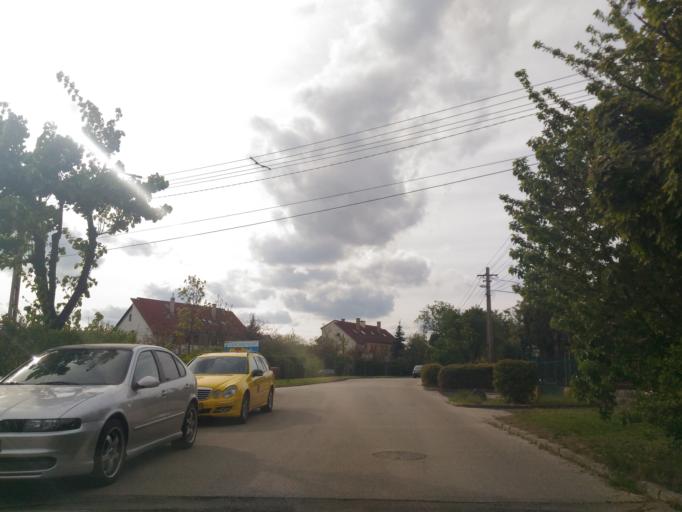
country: HU
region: Budapest
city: Budapest XXII. keruelet
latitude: 47.4246
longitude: 19.0116
